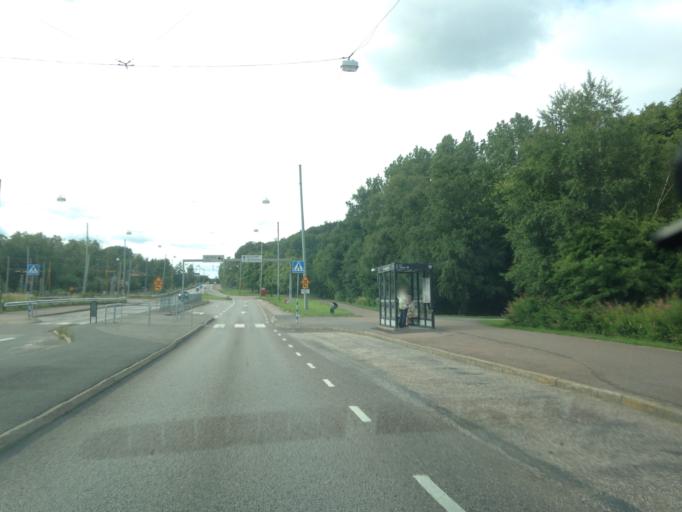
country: SE
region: Vaestra Goetaland
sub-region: Goteborg
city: Goeteborg
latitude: 57.7490
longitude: 11.9501
